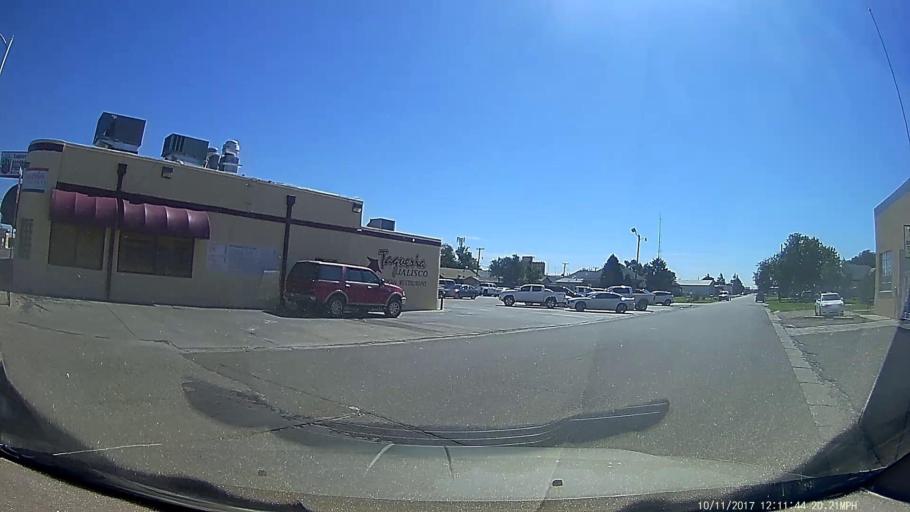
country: US
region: New Mexico
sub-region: Curry County
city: Clovis
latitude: 34.4035
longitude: -103.2078
